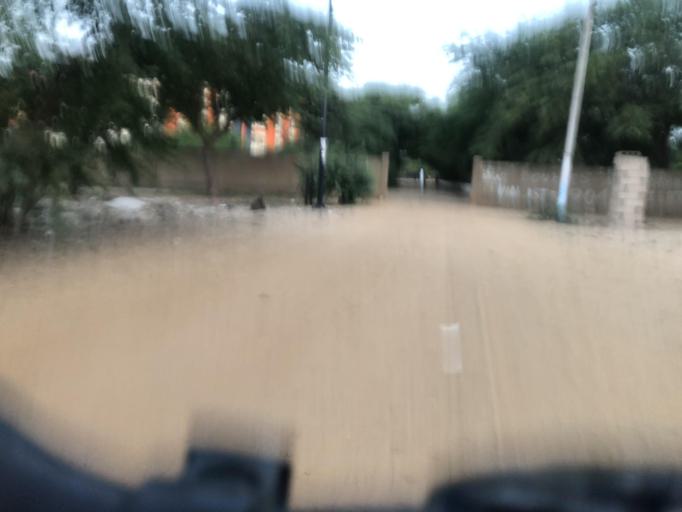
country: SN
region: Saint-Louis
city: Saint-Louis
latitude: 16.0679
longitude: -16.4262
